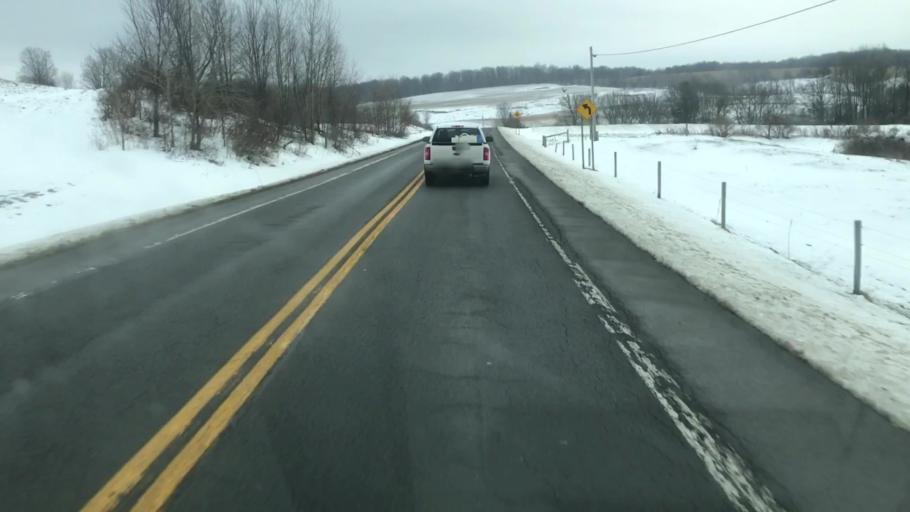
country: US
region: New York
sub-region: Cortland County
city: Cortland West
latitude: 42.6746
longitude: -76.2801
